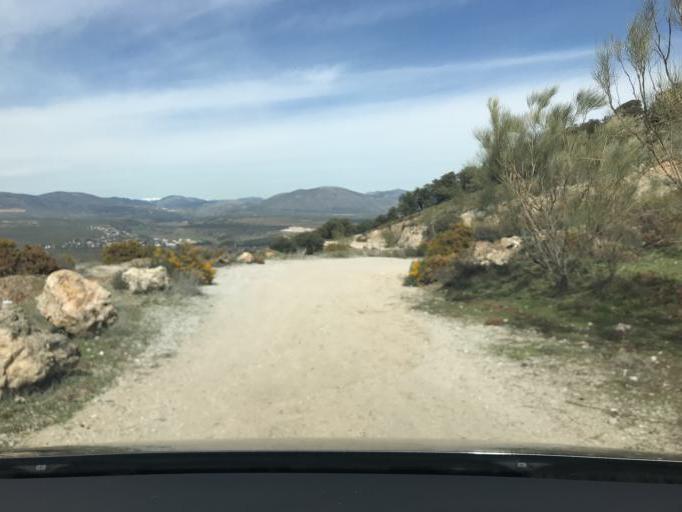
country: ES
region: Andalusia
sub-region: Provincia de Granada
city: Atarfe
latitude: 37.2453
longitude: -3.6880
